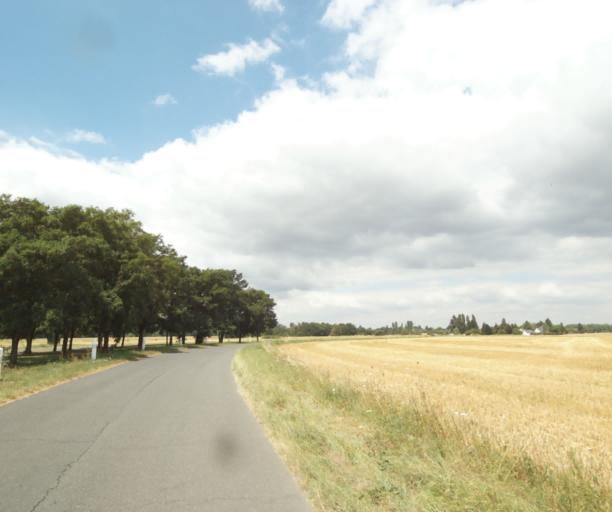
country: FR
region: Centre
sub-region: Departement du Loiret
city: Mardie
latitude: 47.8790
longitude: 2.0411
